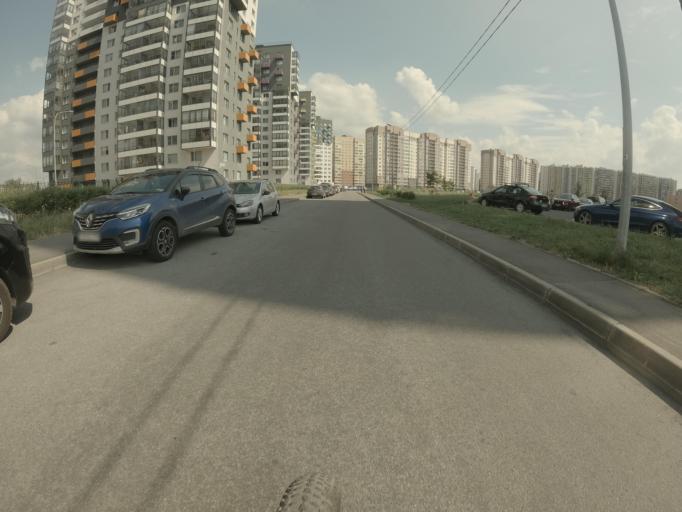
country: RU
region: St.-Petersburg
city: Krasnogvargeisky
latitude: 59.9201
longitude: 30.4353
